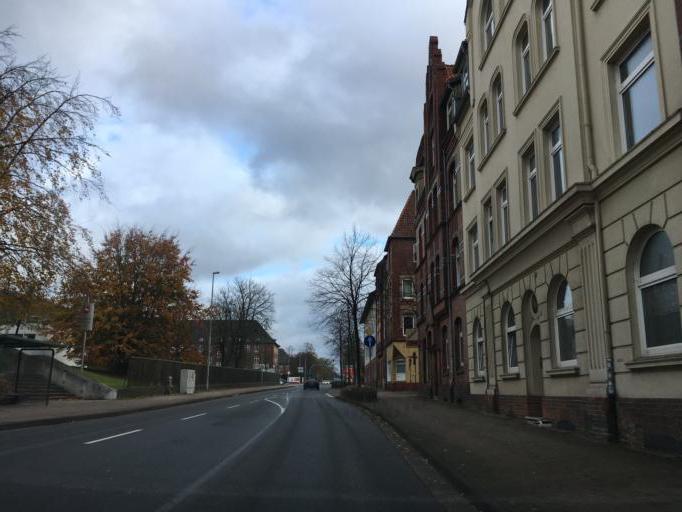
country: DE
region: Lower Saxony
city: Lueneburg
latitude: 53.2510
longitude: 10.4303
